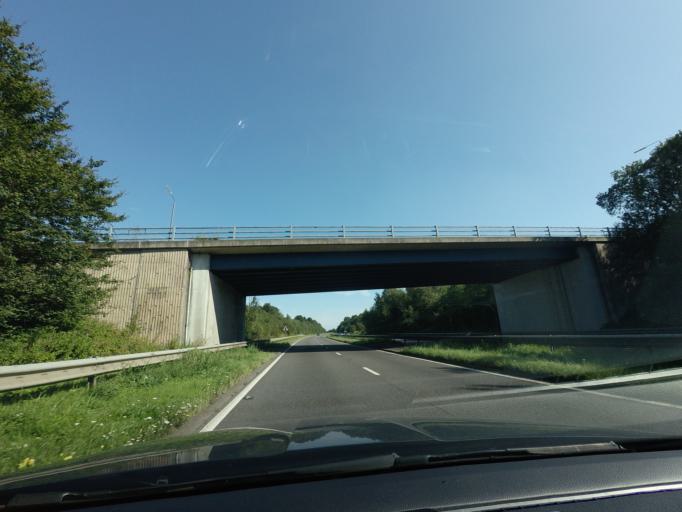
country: GB
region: England
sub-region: Derbyshire
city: Chesterfield
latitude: 53.2088
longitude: -1.3782
